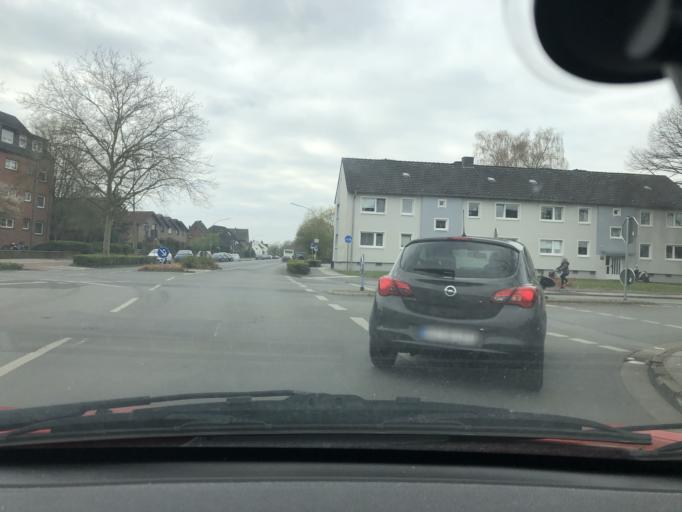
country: DE
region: North Rhine-Westphalia
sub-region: Regierungsbezirk Dusseldorf
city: Kamp-Lintfort
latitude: 51.4959
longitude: 6.5324
